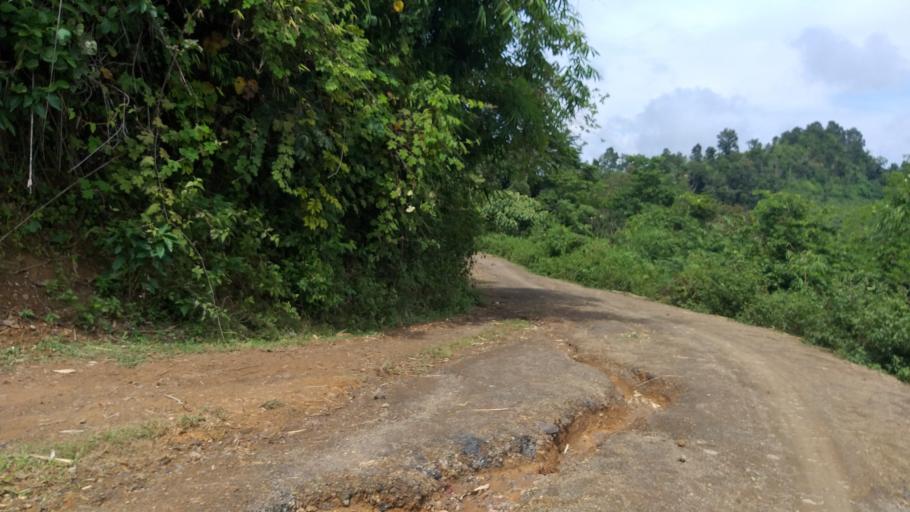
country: VN
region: Huyen Dien Bien
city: Dien Bien Phu
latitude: 21.4472
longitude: 102.6788
